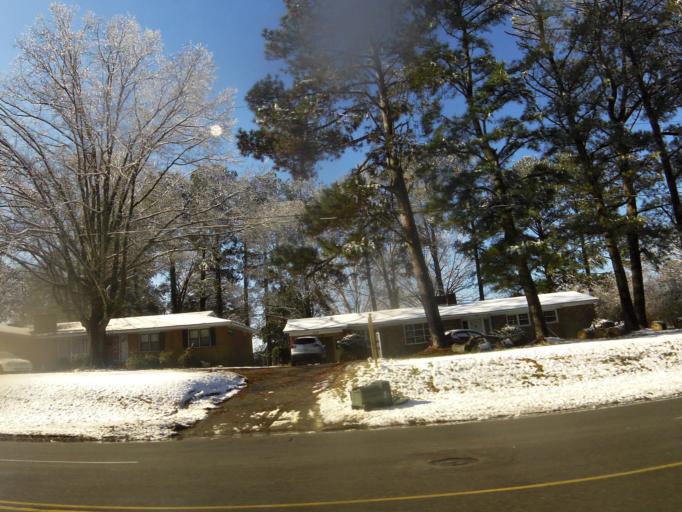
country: US
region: North Carolina
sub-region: Wilson County
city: Wilson
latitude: 35.7251
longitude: -77.8958
